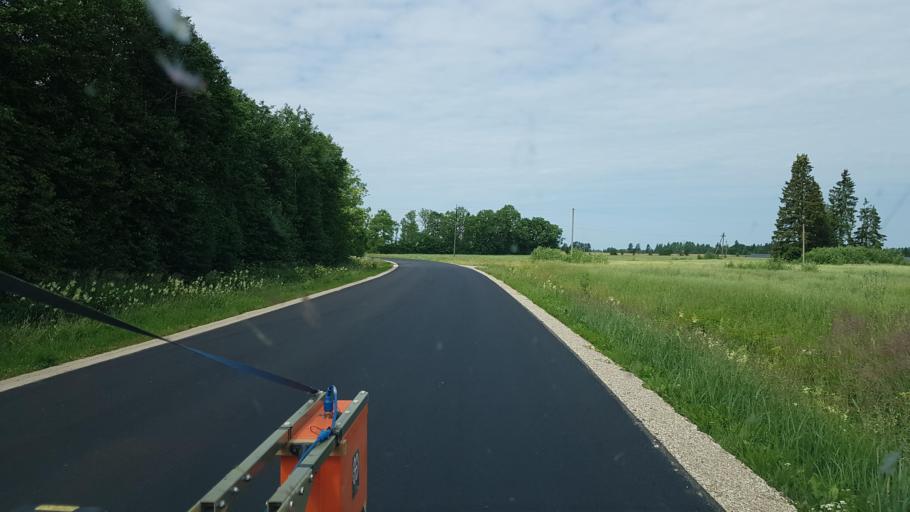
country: EE
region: Paernumaa
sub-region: Halinga vald
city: Parnu-Jaagupi
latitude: 58.6205
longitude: 24.3213
